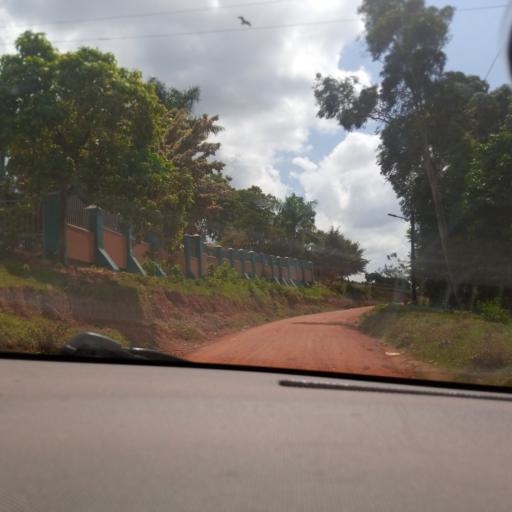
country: UG
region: Central Region
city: Masaka
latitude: -0.3255
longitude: 31.7410
